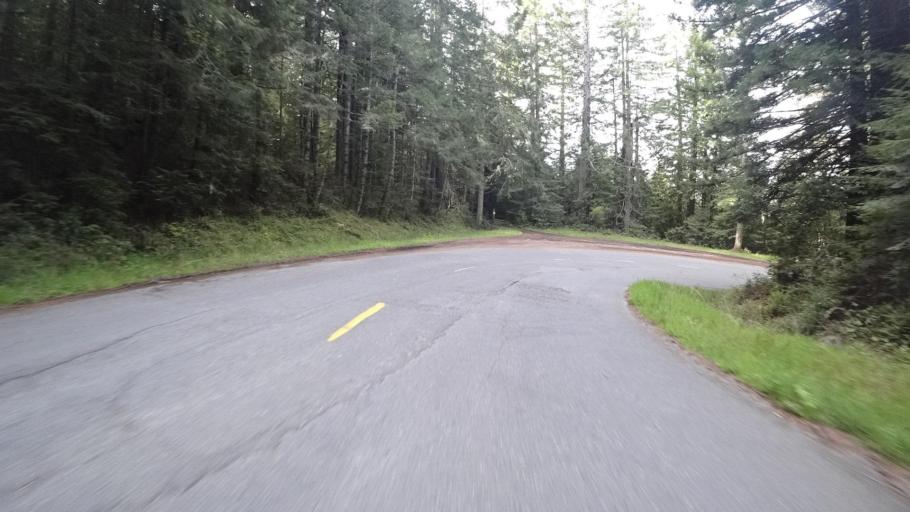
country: US
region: California
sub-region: Humboldt County
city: Bayside
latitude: 40.7565
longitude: -124.0019
